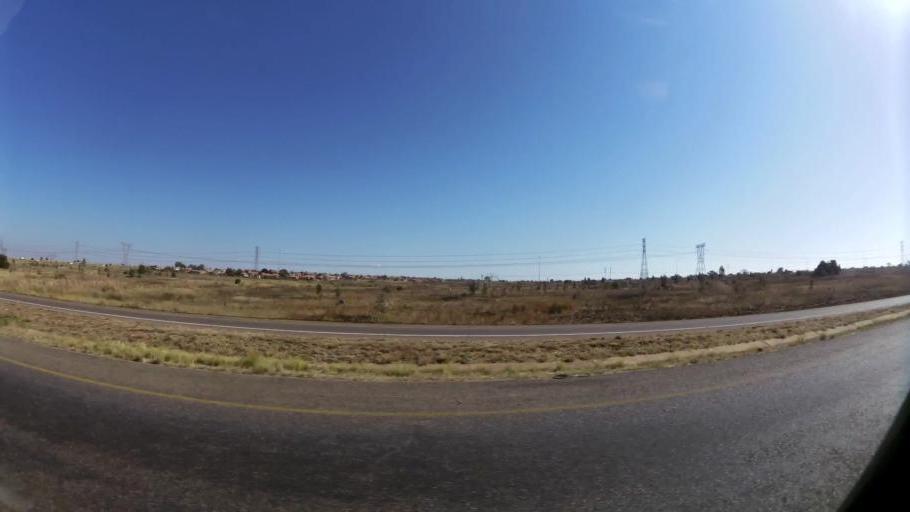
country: ZA
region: Gauteng
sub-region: City of Tshwane Metropolitan Municipality
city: Mabopane
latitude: -25.5533
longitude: 28.1087
